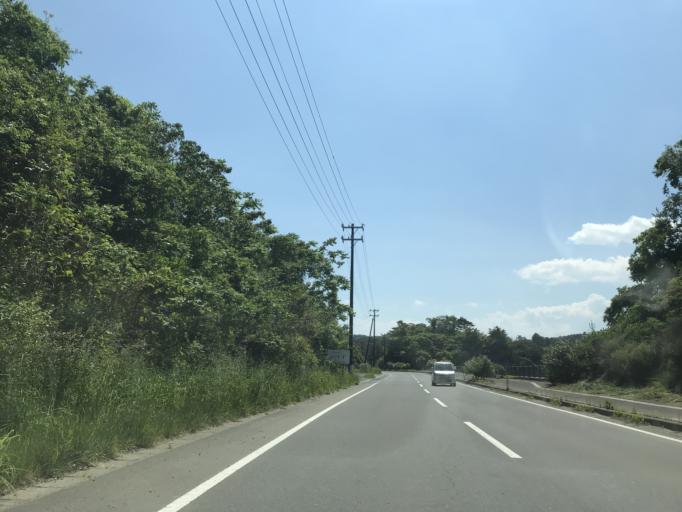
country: JP
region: Miyagi
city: Matsushima
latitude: 38.3412
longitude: 141.1491
